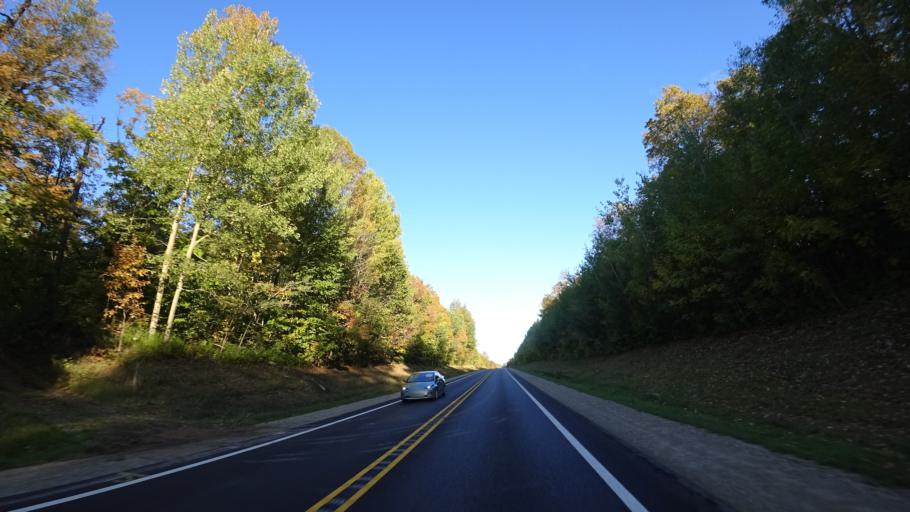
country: US
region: Michigan
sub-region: Luce County
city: Newberry
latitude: 46.3355
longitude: -85.8090
